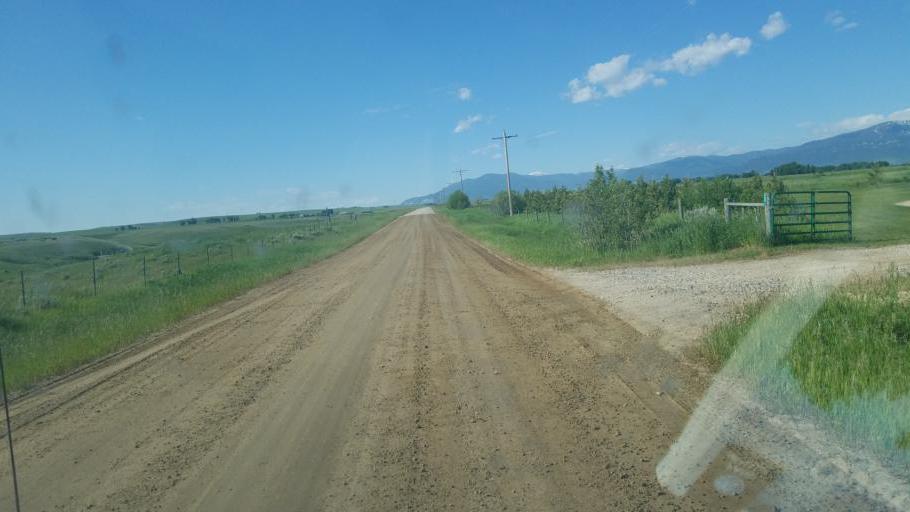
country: US
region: Montana
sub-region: Carbon County
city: Red Lodge
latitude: 45.3094
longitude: -109.1784
